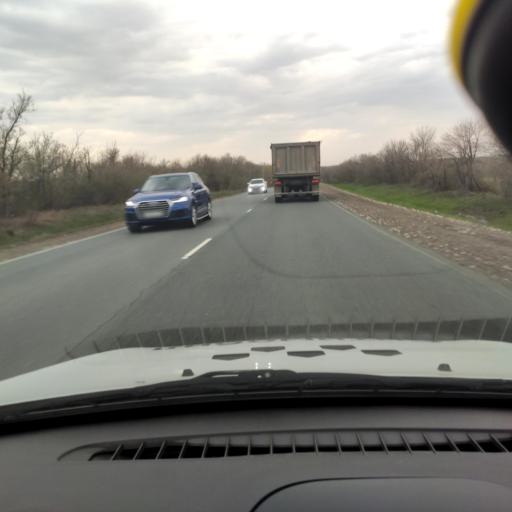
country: RU
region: Samara
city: Zhigulevsk
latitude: 53.3029
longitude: 49.3470
